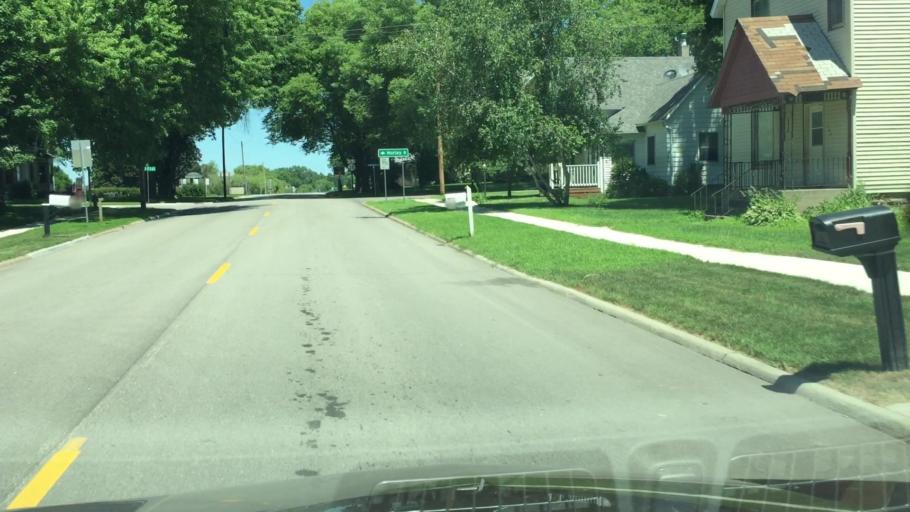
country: US
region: Iowa
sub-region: Cedar County
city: Mechanicsville
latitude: 42.0001
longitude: -91.1419
